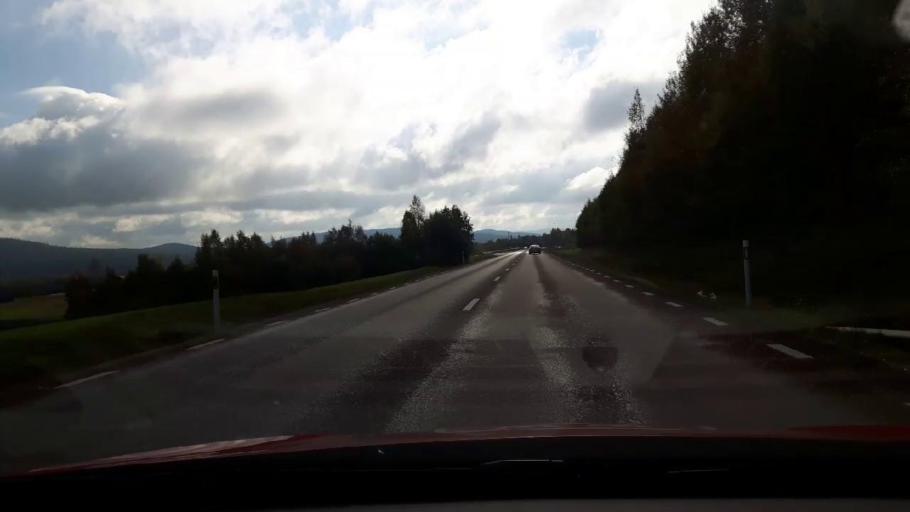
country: SE
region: Gaevleborg
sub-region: Ljusdals Kommun
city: Jaervsoe
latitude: 61.7308
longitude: 16.1655
